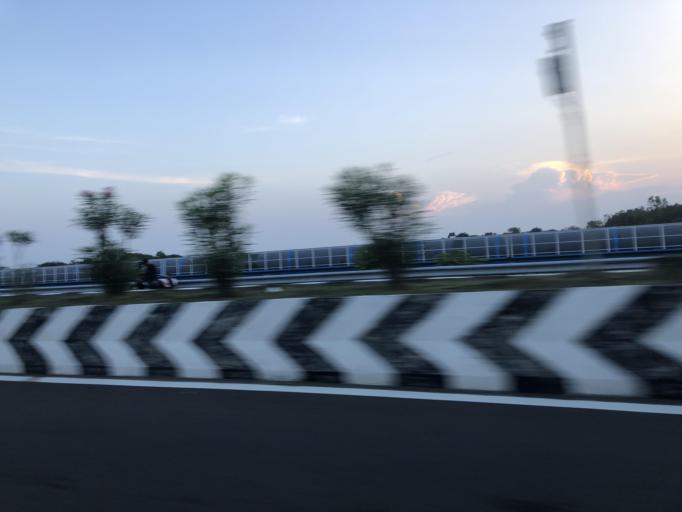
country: IN
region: Tamil Nadu
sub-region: Kancheepuram
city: Injambakkam
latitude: 12.7875
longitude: 80.2438
